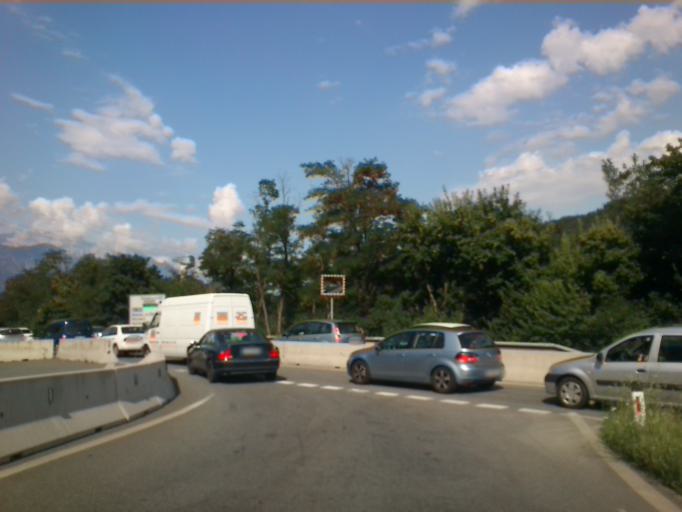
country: AT
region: Tyrol
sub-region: Politischer Bezirk Innsbruck Land
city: Mutters
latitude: 47.2410
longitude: 11.3894
